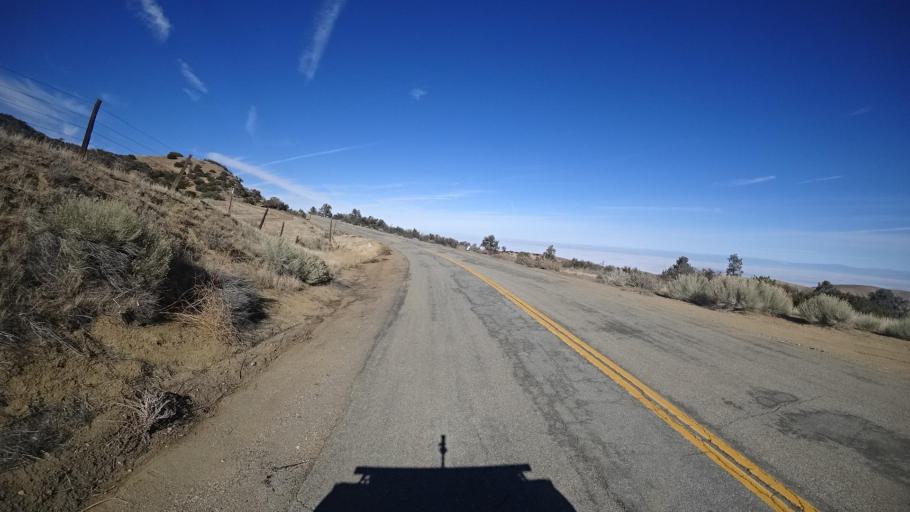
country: US
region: California
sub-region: Kern County
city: Maricopa
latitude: 34.8911
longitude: -119.3563
